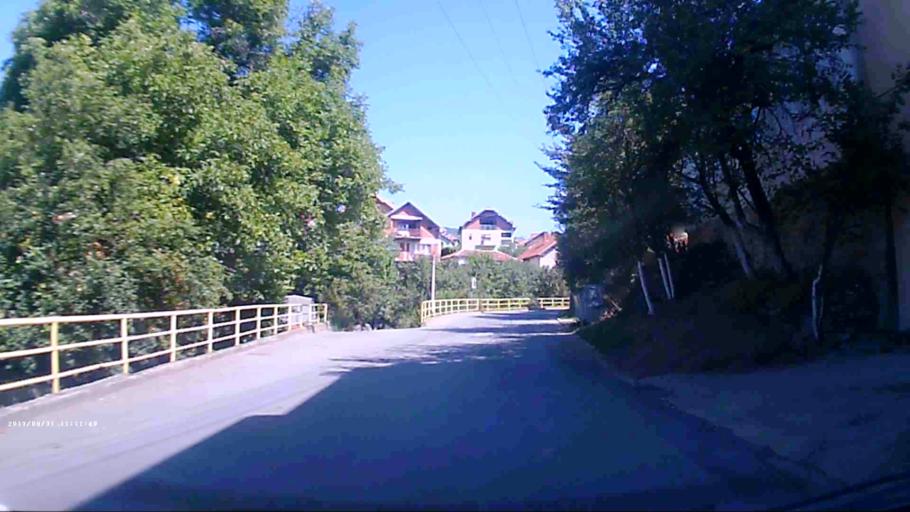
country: RS
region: Central Serbia
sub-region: Pirotski Okrug
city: Dimitrovgrad
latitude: 43.0186
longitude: 22.7820
